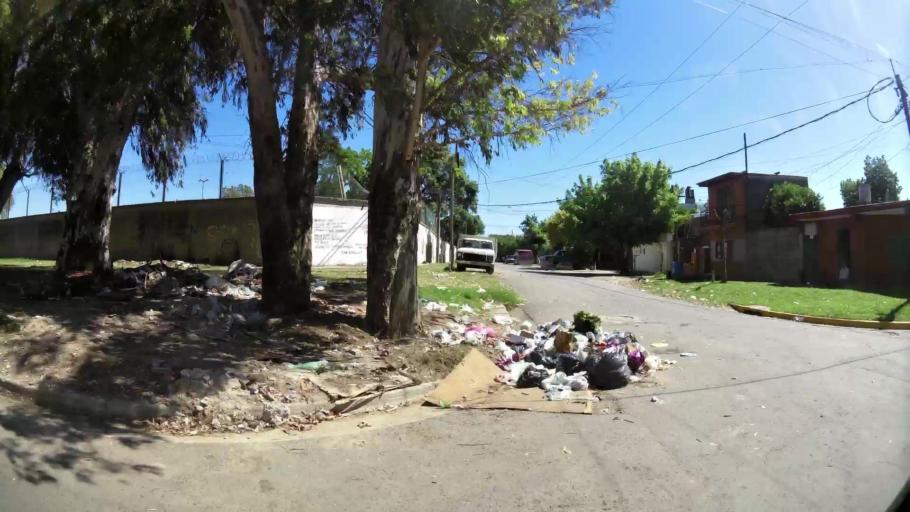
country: AR
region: Santa Fe
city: Perez
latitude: -32.9695
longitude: -60.7080
